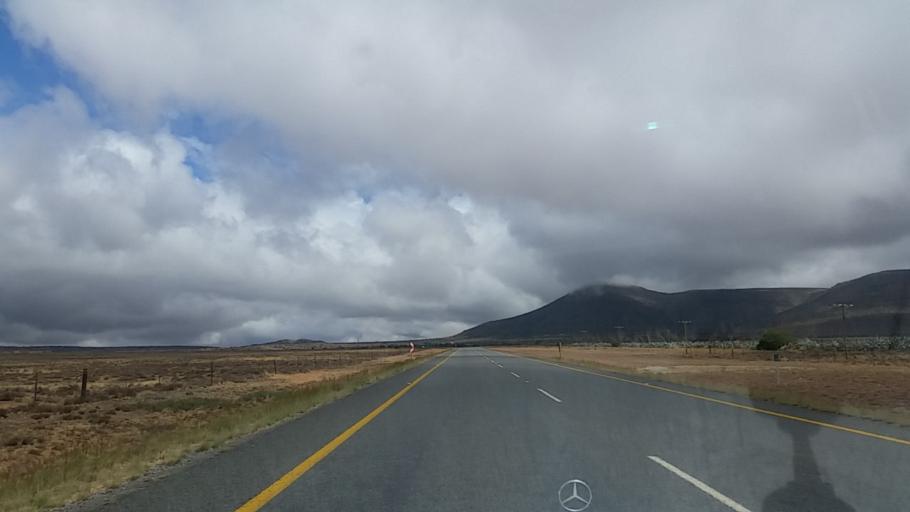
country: ZA
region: Eastern Cape
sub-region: Cacadu District Municipality
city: Graaff-Reinet
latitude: -32.0261
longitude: 24.6317
